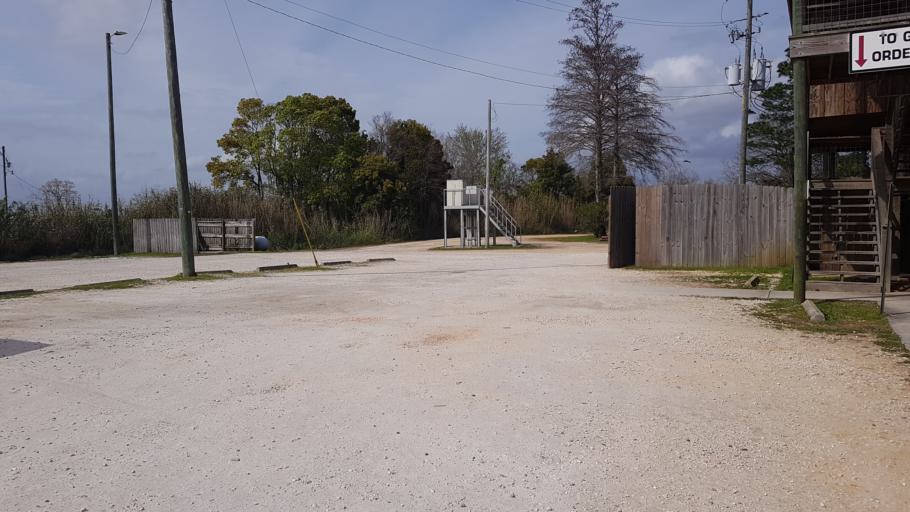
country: US
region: Alabama
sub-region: Mobile County
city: Mobile
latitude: 30.6804
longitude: -87.9974
